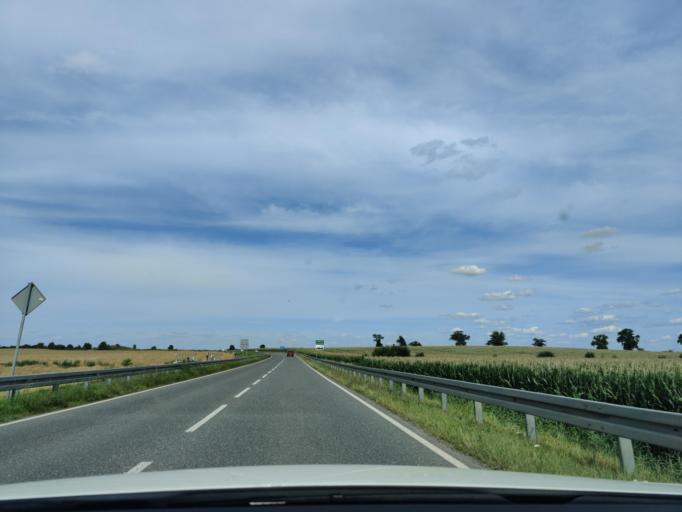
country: PL
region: Opole Voivodeship
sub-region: Powiat prudnicki
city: Biala
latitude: 50.4164
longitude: 17.7237
